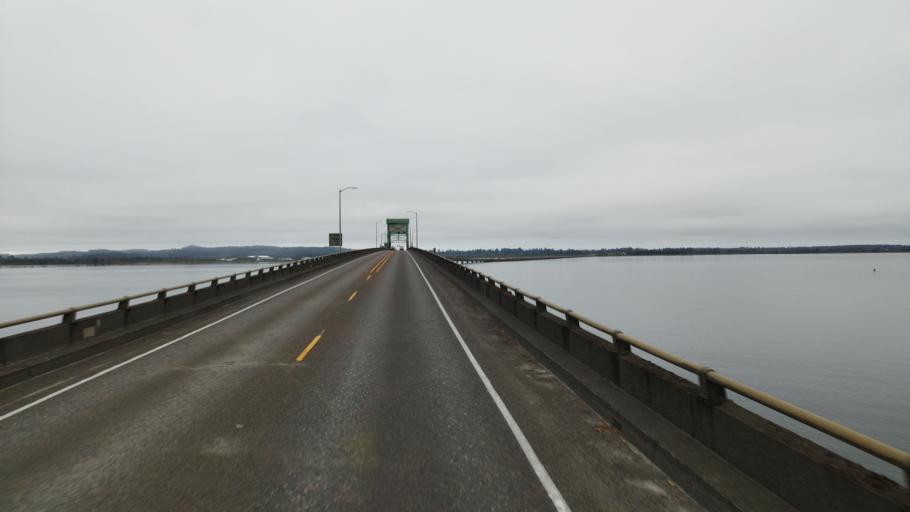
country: US
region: Oregon
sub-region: Clatsop County
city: Astoria
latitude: 46.1788
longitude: -123.8652
